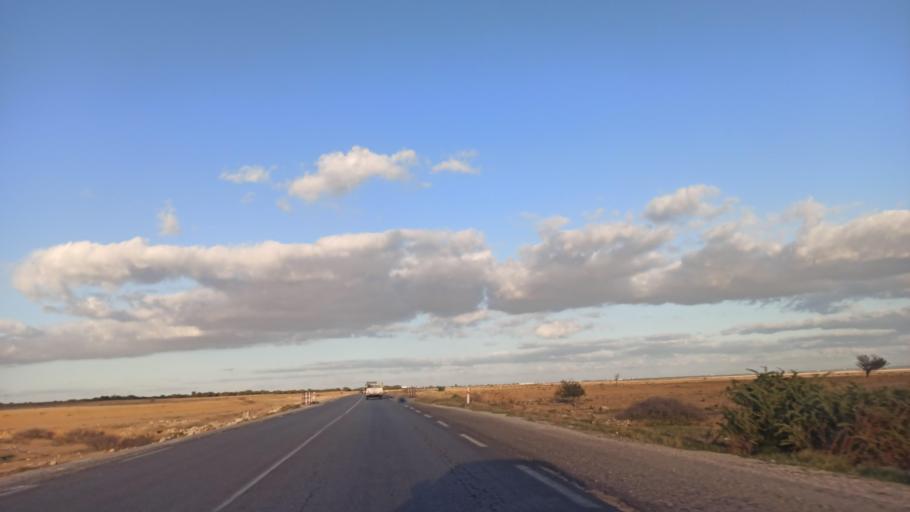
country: TN
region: Susah
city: Sidi Bou Ali
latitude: 35.8958
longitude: 10.2541
